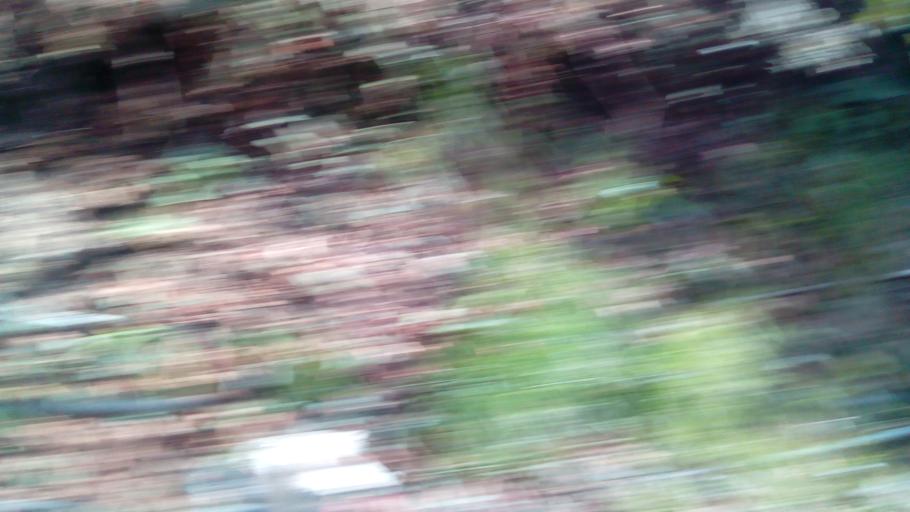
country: TW
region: Taiwan
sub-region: Hualien
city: Hualian
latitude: 24.3306
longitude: 121.3110
